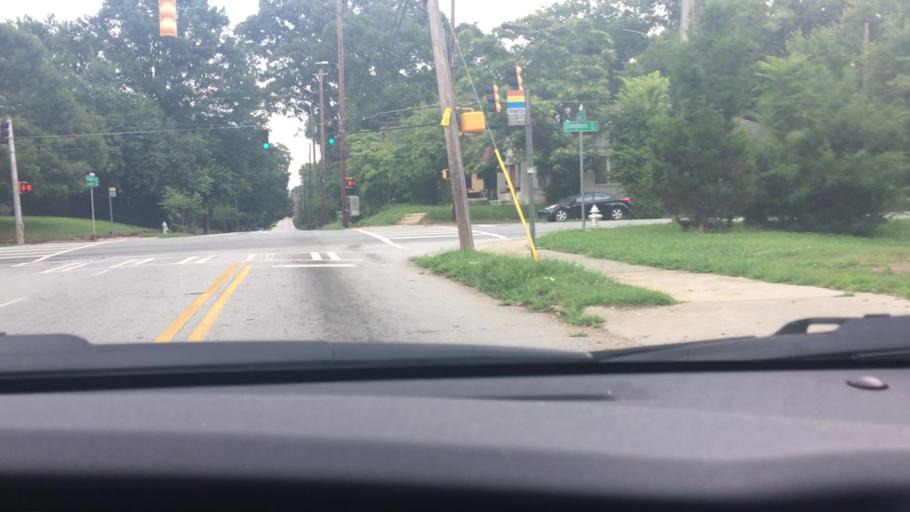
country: US
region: Georgia
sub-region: Fulton County
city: Atlanta
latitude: 33.7423
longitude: -84.4328
